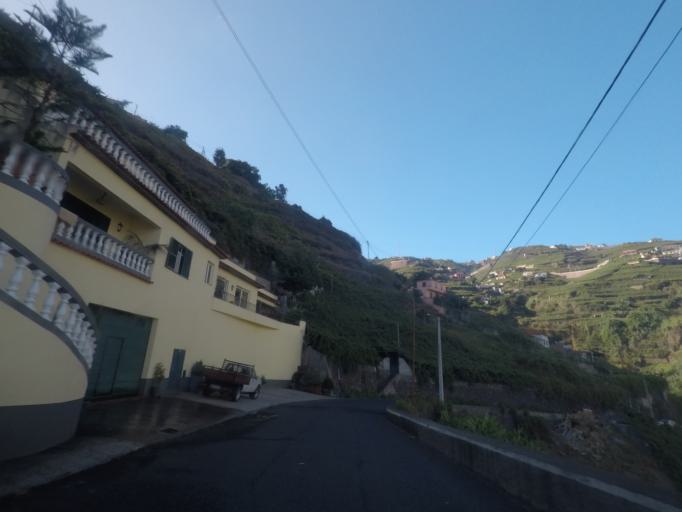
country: PT
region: Madeira
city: Camara de Lobos
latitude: 32.6701
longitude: -16.9864
